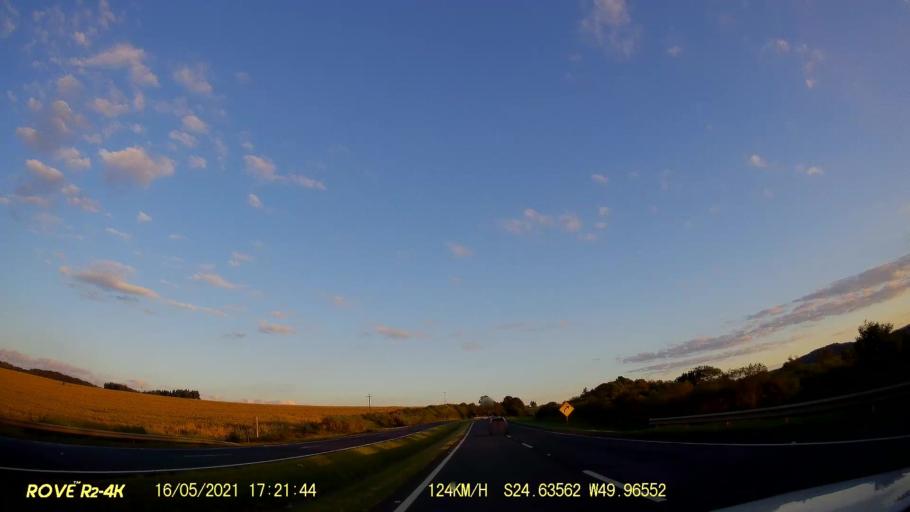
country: BR
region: Parana
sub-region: Pirai Do Sul
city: Pirai do Sul
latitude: -24.6360
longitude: -49.9655
